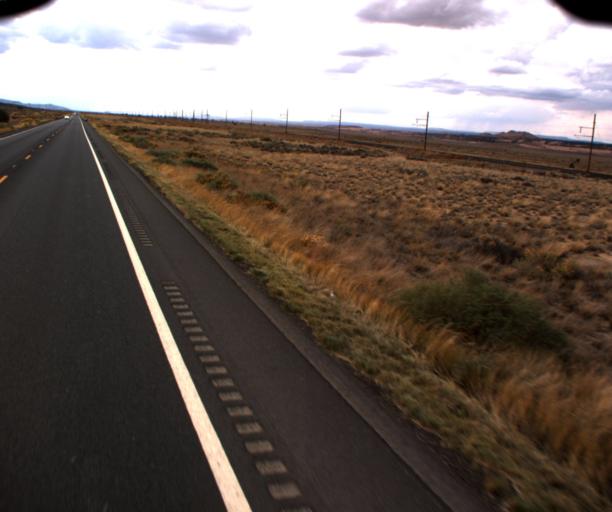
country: US
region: Arizona
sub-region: Navajo County
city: Kayenta
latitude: 36.5292
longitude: -110.5708
